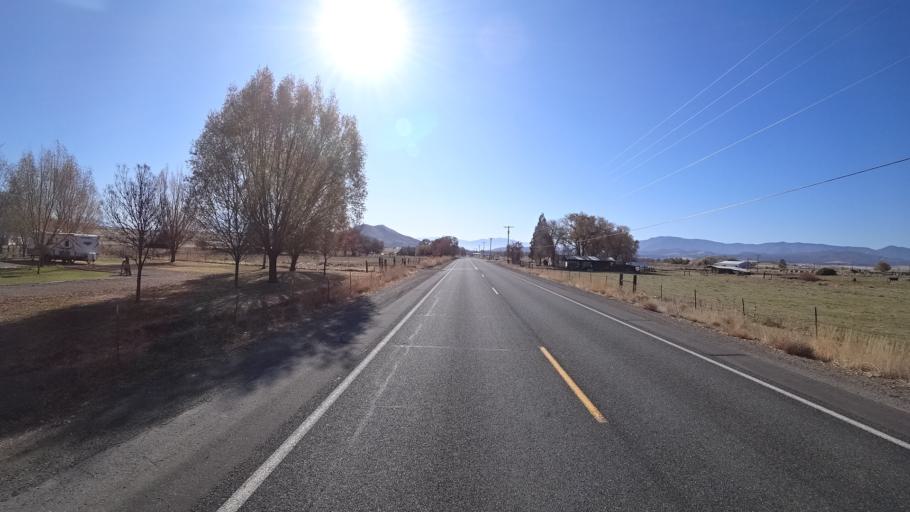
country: US
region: California
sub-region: Siskiyou County
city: Montague
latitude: 41.7433
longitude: -122.5246
